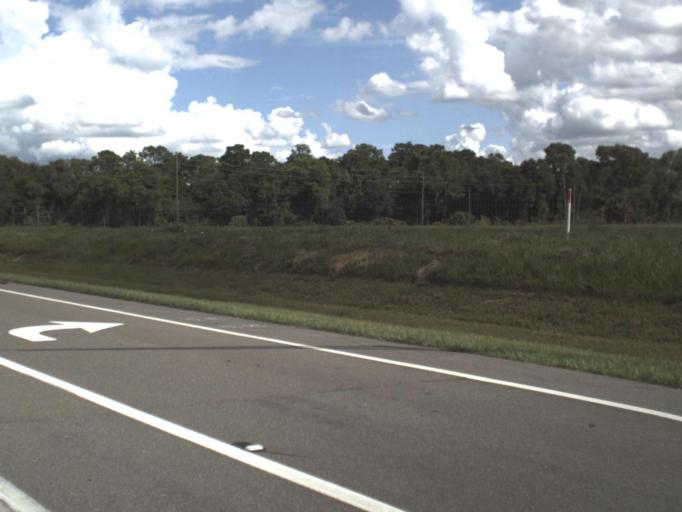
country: US
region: Florida
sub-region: Polk County
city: Jan-Phyl Village
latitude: 28.0102
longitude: -81.8227
